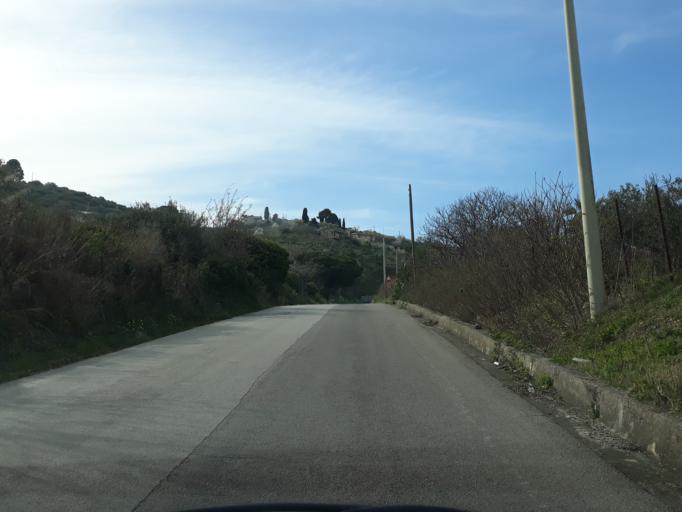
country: IT
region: Sicily
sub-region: Palermo
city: Piano Maglio-Blandino
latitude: 38.0401
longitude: 13.3127
